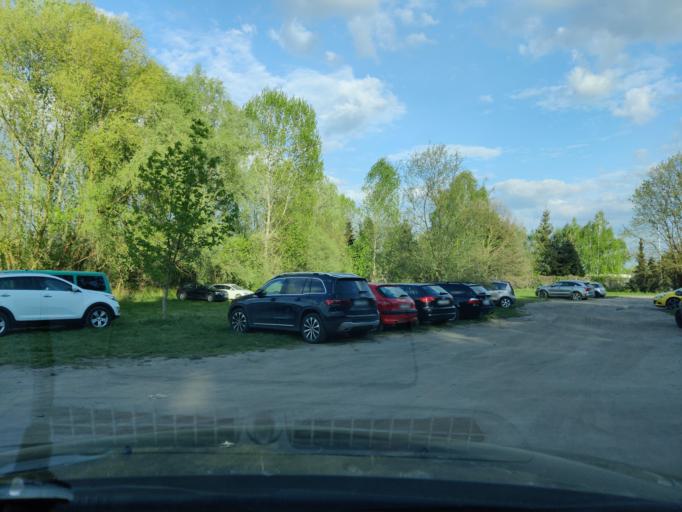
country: PL
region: Masovian Voivodeship
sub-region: Warszawa
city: Kabaty
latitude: 52.1178
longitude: 21.0927
